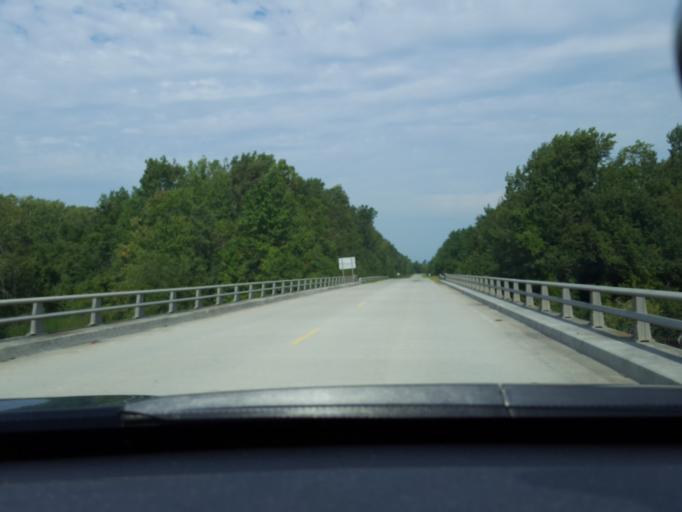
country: US
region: North Carolina
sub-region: Washington County
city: Plymouth
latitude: 35.9238
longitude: -76.7333
